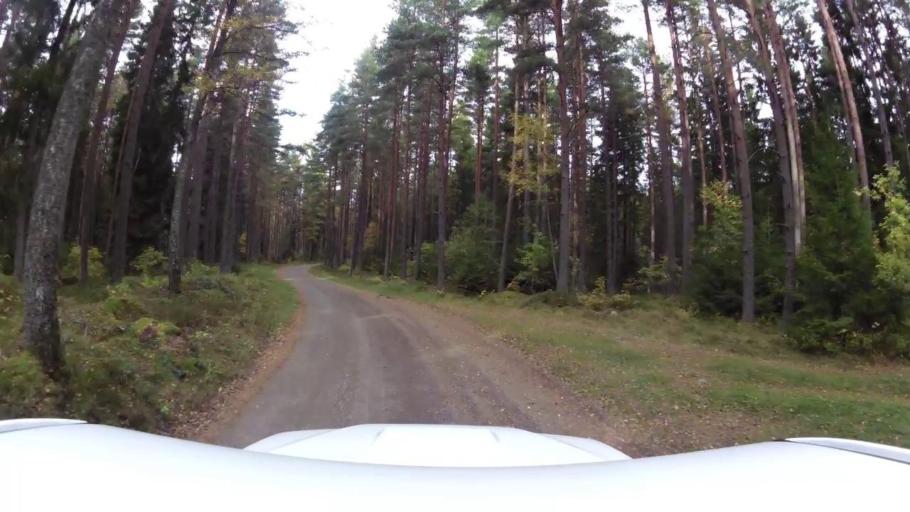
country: SE
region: OEstergoetland
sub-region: Linkopings Kommun
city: Ekangen
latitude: 58.5546
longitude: 15.6728
